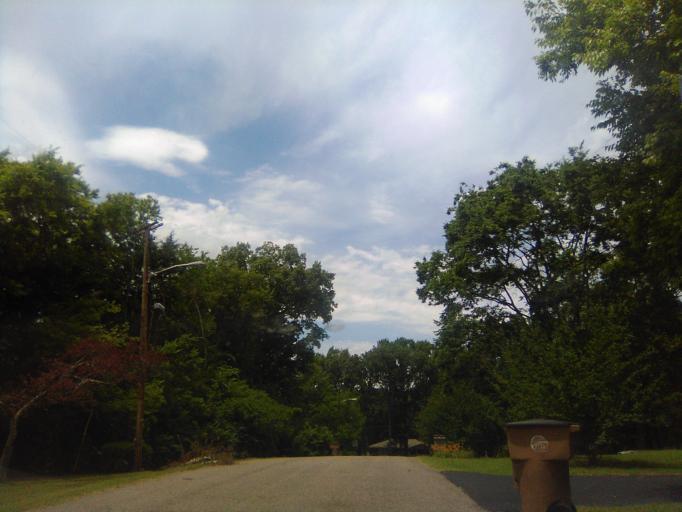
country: US
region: Tennessee
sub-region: Davidson County
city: Belle Meade
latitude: 36.1291
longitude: -86.8873
